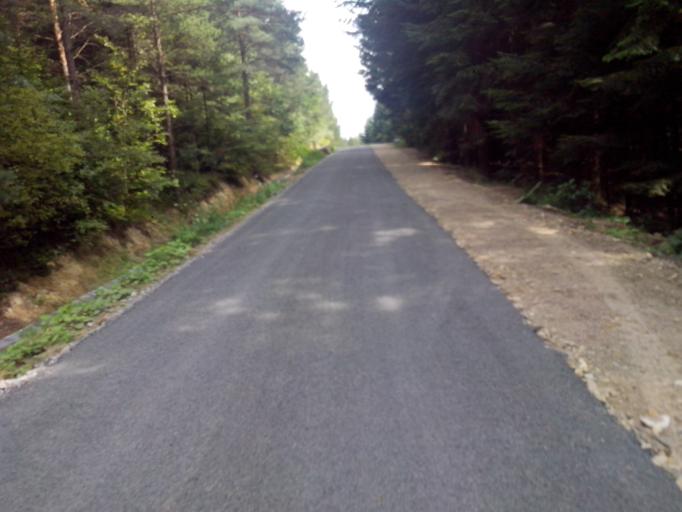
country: PL
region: Subcarpathian Voivodeship
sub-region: Powiat strzyzowski
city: Strzyzow
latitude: 49.8123
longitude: 21.7979
